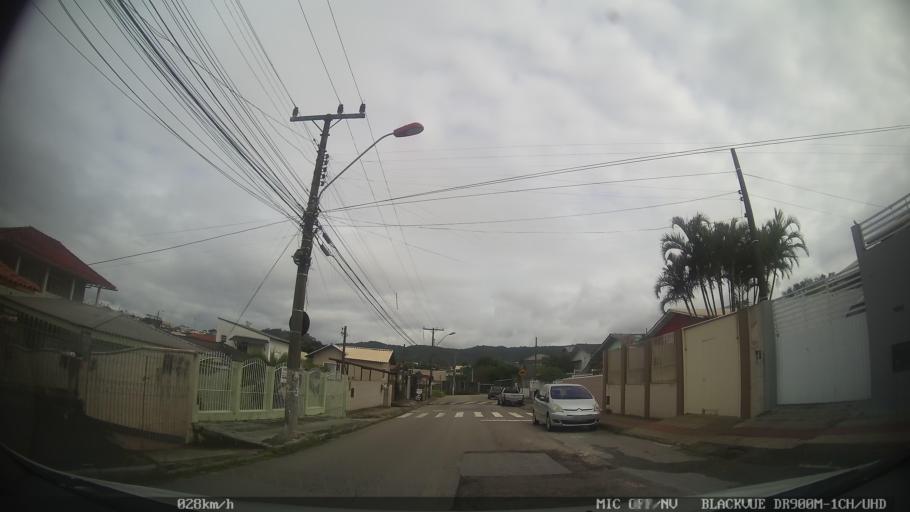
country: BR
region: Santa Catarina
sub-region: Biguacu
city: Biguacu
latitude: -27.5387
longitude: -48.6328
